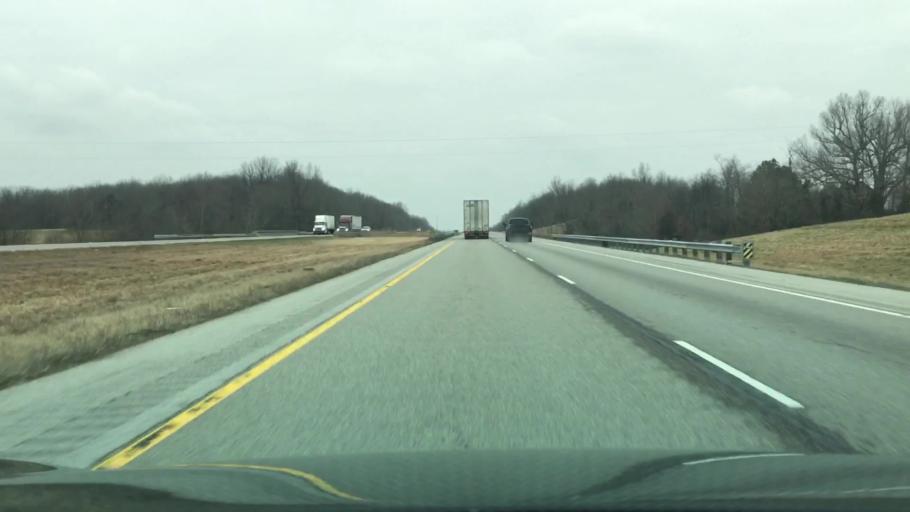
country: US
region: Illinois
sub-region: Massac County
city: Metropolis
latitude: 37.2151
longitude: -88.6991
